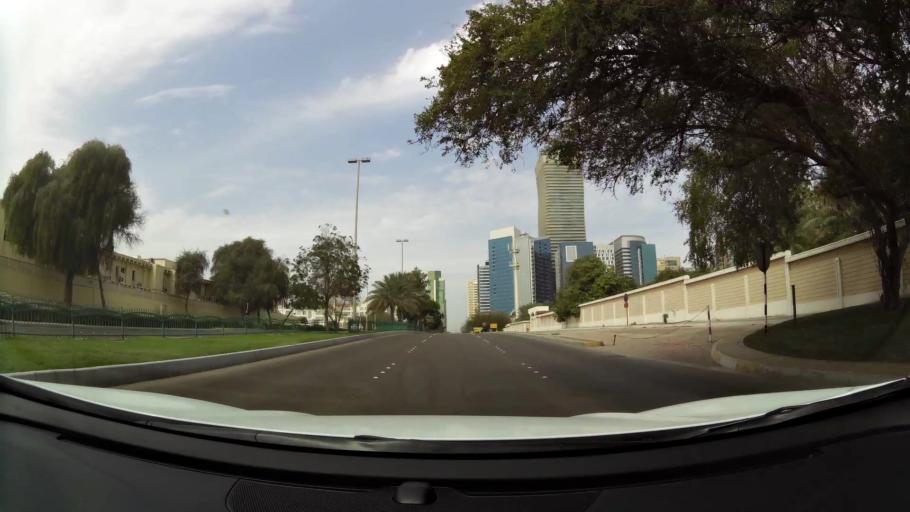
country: AE
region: Abu Dhabi
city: Abu Dhabi
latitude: 24.4646
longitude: 54.3420
